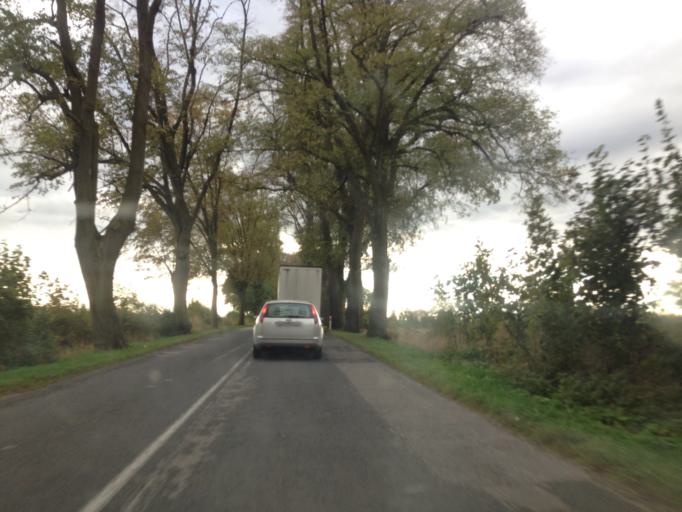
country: PL
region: Pomeranian Voivodeship
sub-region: Powiat kwidzynski
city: Kwidzyn
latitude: 53.7348
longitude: 19.0587
